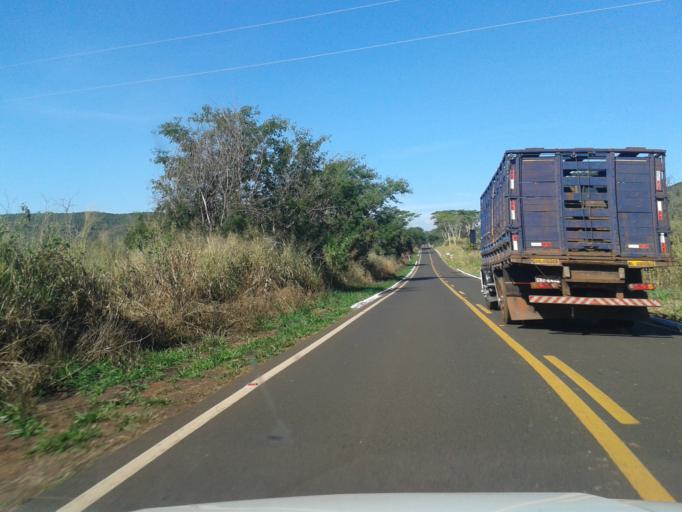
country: BR
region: Minas Gerais
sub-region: Ituiutaba
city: Ituiutaba
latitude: -19.1724
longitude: -49.7803
